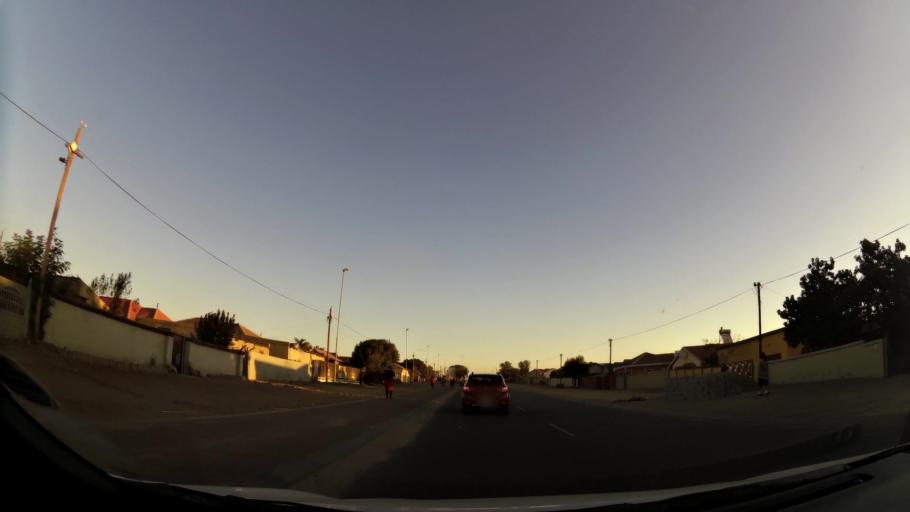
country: ZA
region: Limpopo
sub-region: Capricorn District Municipality
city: Polokwane
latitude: -23.8555
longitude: 29.3767
